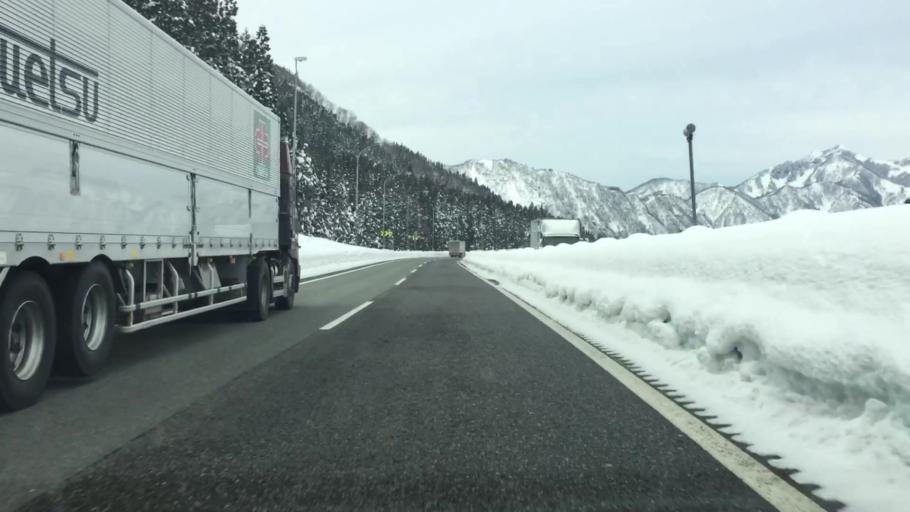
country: JP
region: Niigata
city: Shiozawa
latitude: 36.8915
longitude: 138.8470
